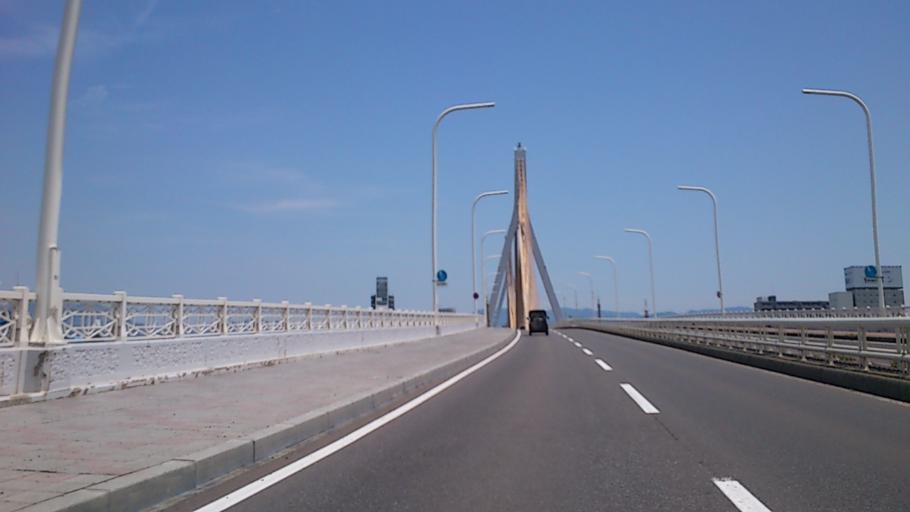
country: JP
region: Aomori
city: Aomori Shi
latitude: 40.8318
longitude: 140.7320
